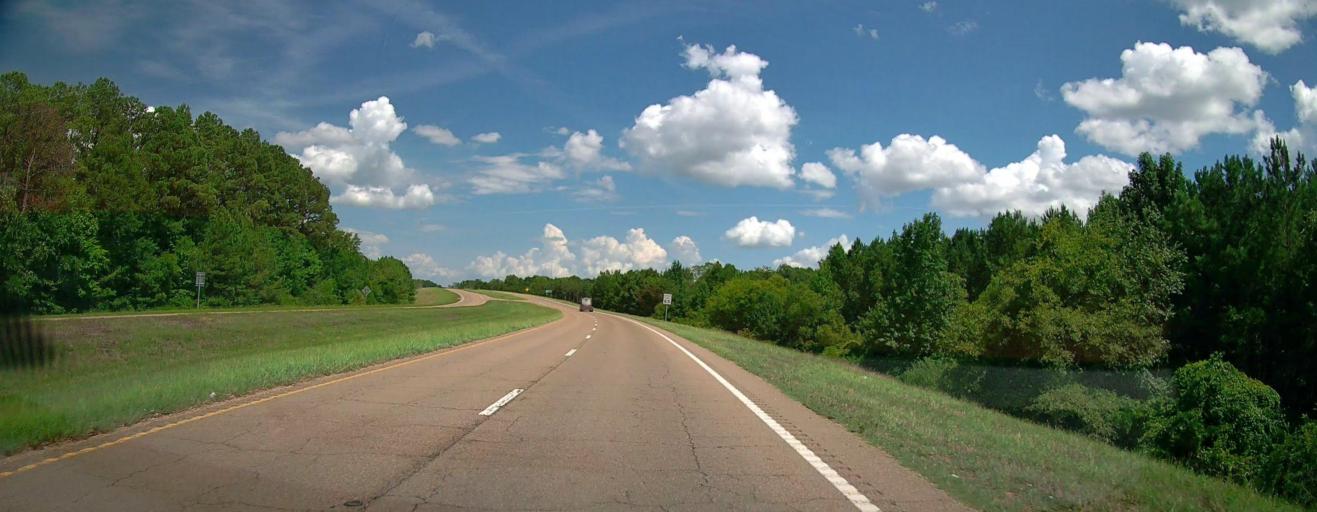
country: US
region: Mississippi
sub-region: Monroe County
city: Aberdeen
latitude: 33.8102
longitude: -88.4855
